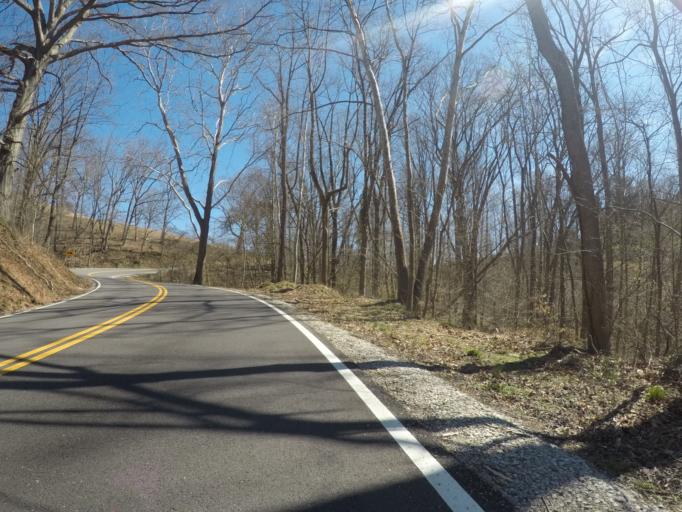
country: US
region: Ohio
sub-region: Lawrence County
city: South Point
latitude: 38.4586
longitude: -82.5533
